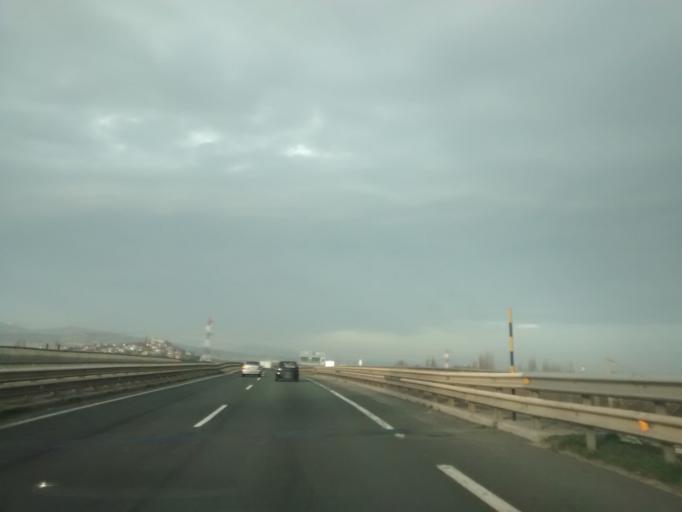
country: ES
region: Basque Country
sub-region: Provincia de Alava
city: Gasteiz / Vitoria
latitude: 42.8511
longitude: -2.7471
